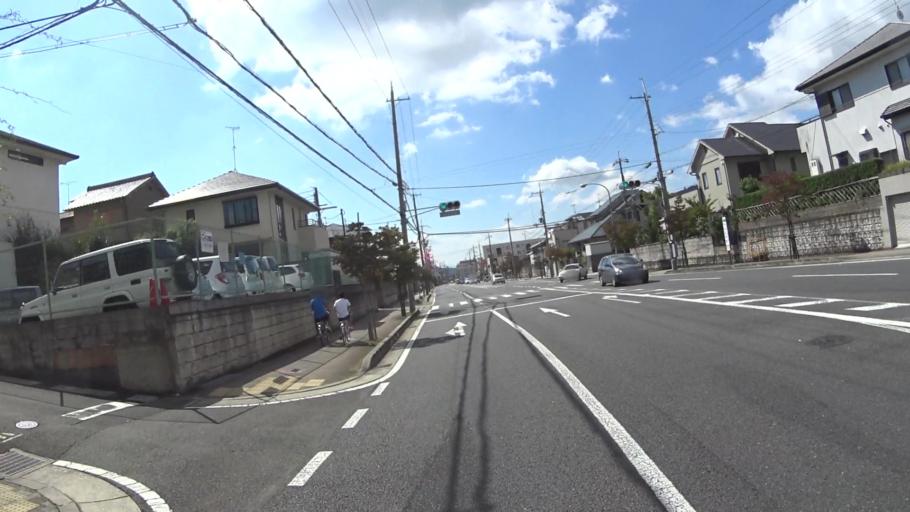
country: JP
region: Kyoto
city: Muko
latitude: 34.9207
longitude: 135.6892
